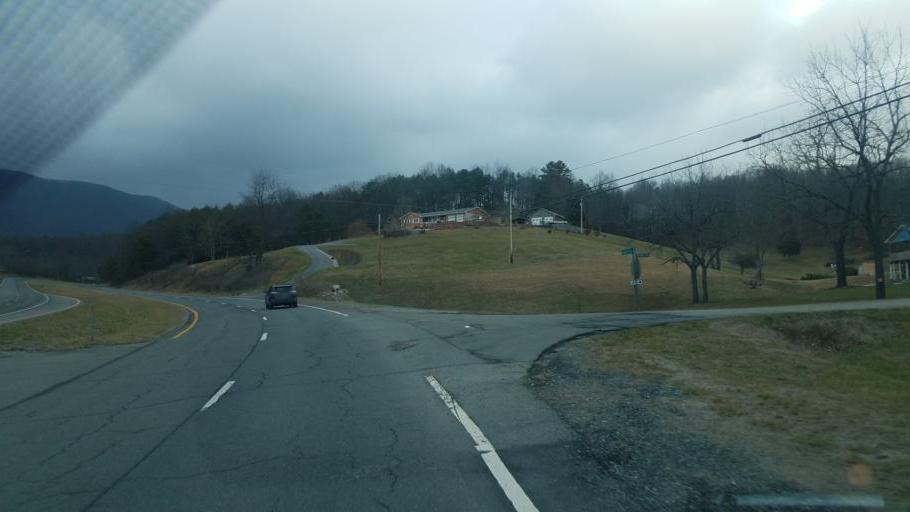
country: US
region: Virginia
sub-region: Giles County
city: Pearisburg
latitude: 37.2801
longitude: -80.7420
